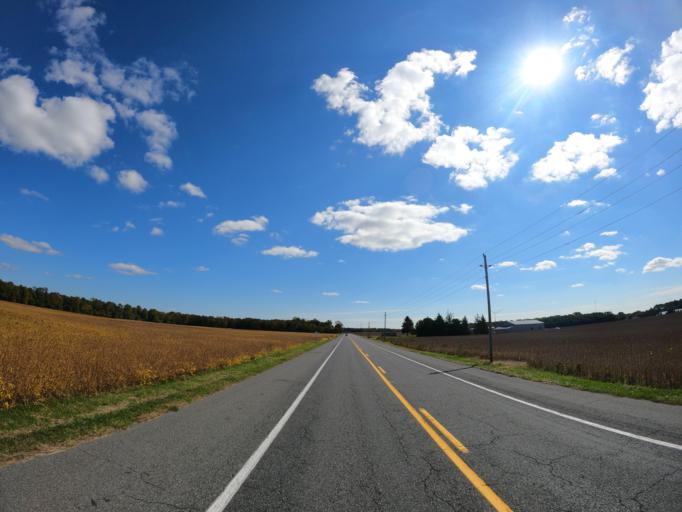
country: US
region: Delaware
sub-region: Sussex County
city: Bridgeville
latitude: 38.8284
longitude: -75.6602
